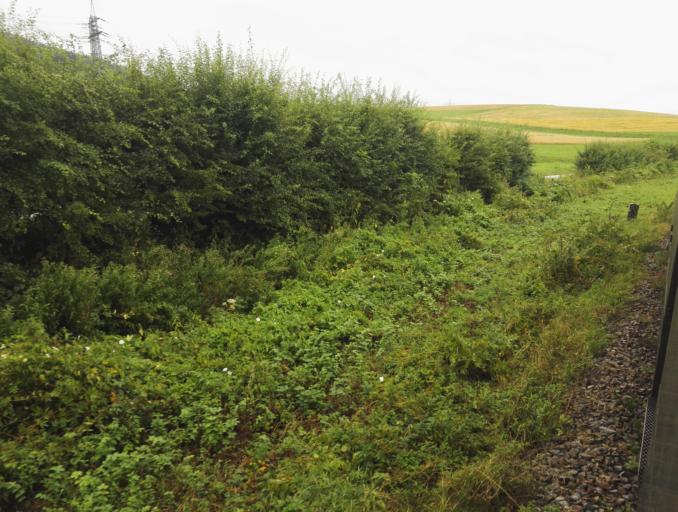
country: DE
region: Baden-Wuerttemberg
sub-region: Freiburg Region
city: Blumberg
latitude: 47.8136
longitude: 8.5414
